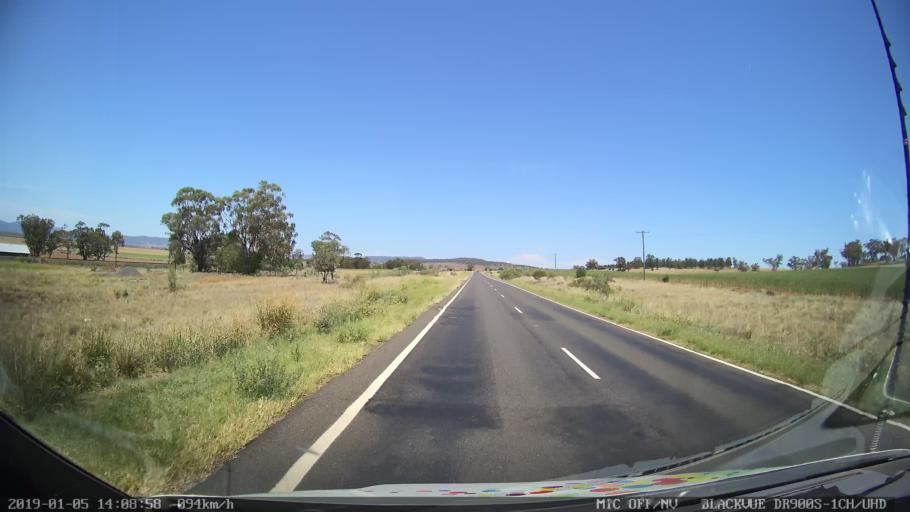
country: AU
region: New South Wales
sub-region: Gunnedah
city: Gunnedah
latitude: -31.2393
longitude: 150.4200
